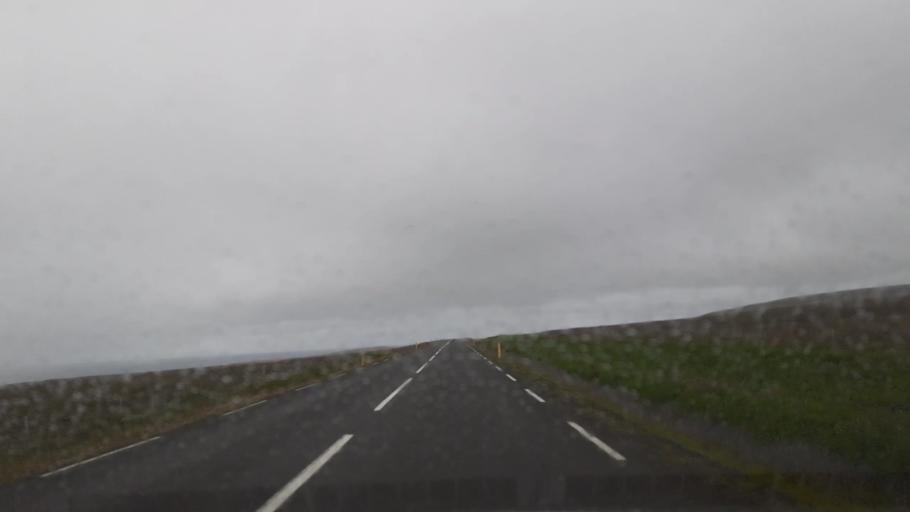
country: IS
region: Northeast
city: Husavik
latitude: 66.1328
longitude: -17.2352
